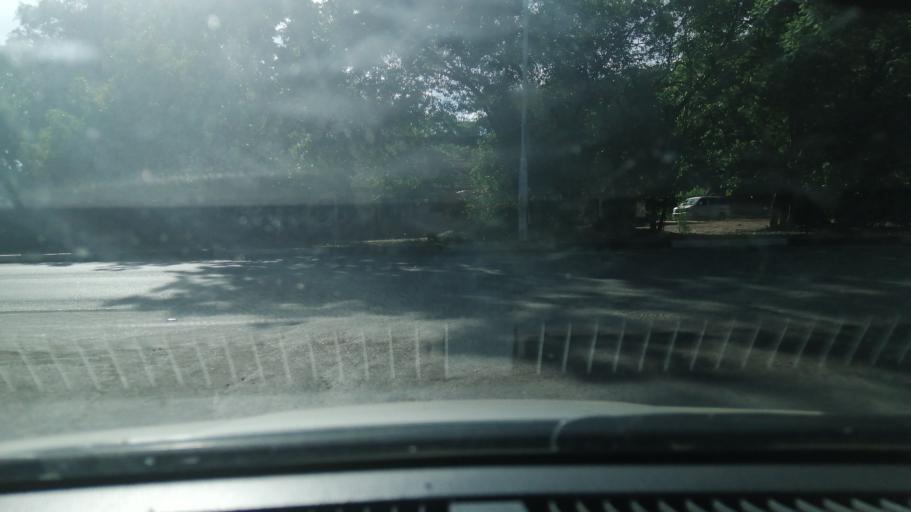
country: ZW
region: Harare
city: Harare
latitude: -17.7644
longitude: 31.0517
